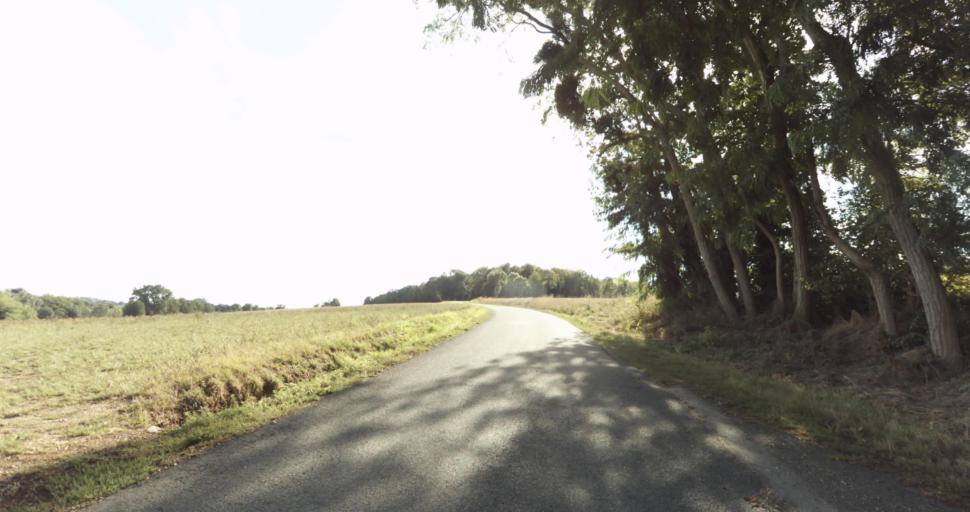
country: FR
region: Lower Normandy
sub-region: Departement de l'Orne
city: Vimoutiers
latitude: 48.9237
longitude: 0.1243
